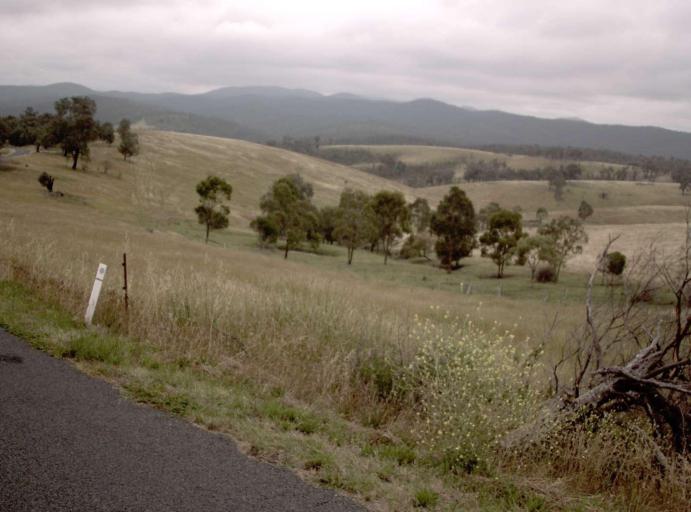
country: AU
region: Victoria
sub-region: Wellington
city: Heyfield
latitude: -37.8694
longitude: 146.7066
